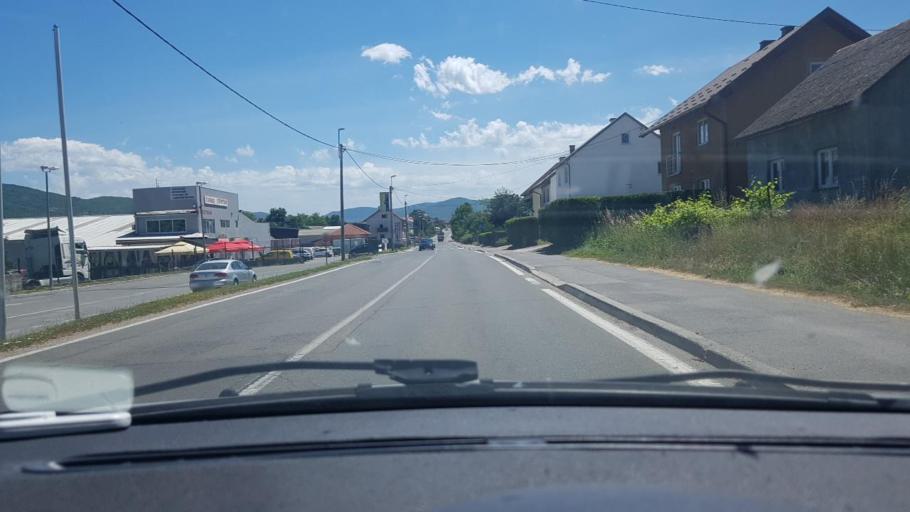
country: HR
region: Licko-Senjska
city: Otocac
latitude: 44.8678
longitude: 15.2496
